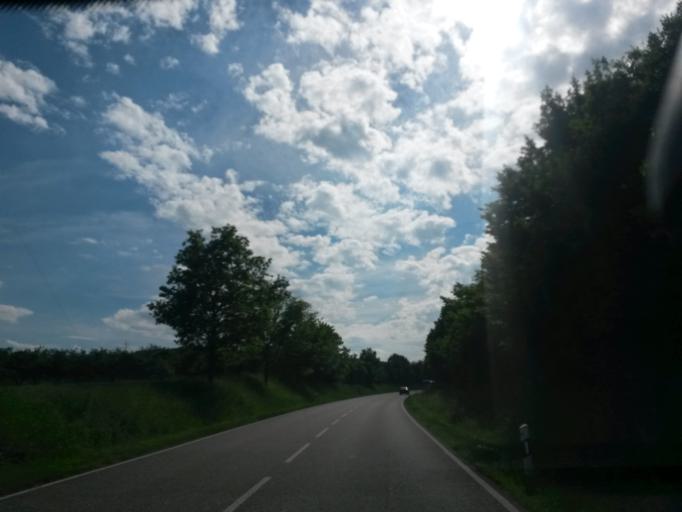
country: DE
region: Baden-Wuerttemberg
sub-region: Karlsruhe Region
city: Simmozheim
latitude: 48.7480
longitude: 8.8207
